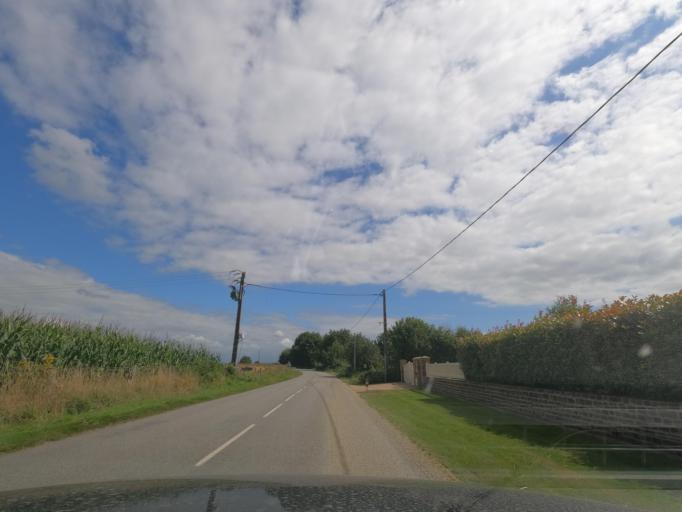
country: FR
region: Pays de la Loire
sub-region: Departement de la Mayenne
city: Landivy
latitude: 48.4786
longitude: -1.0189
